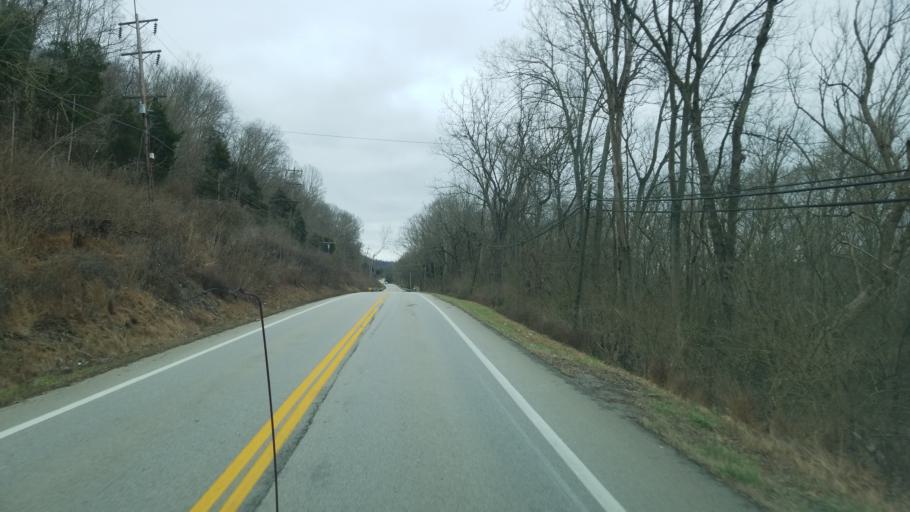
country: US
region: Ohio
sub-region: Clermont County
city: New Richmond
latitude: 38.9096
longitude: -84.2460
